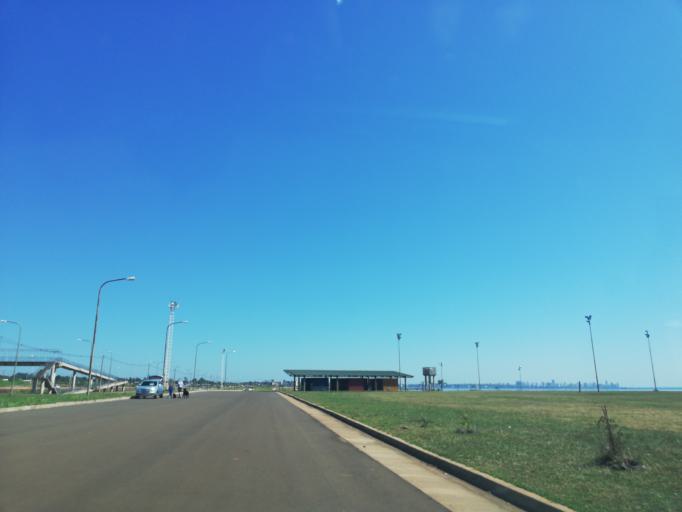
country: AR
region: Misiones
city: Garupa
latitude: -27.4327
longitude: -55.8627
